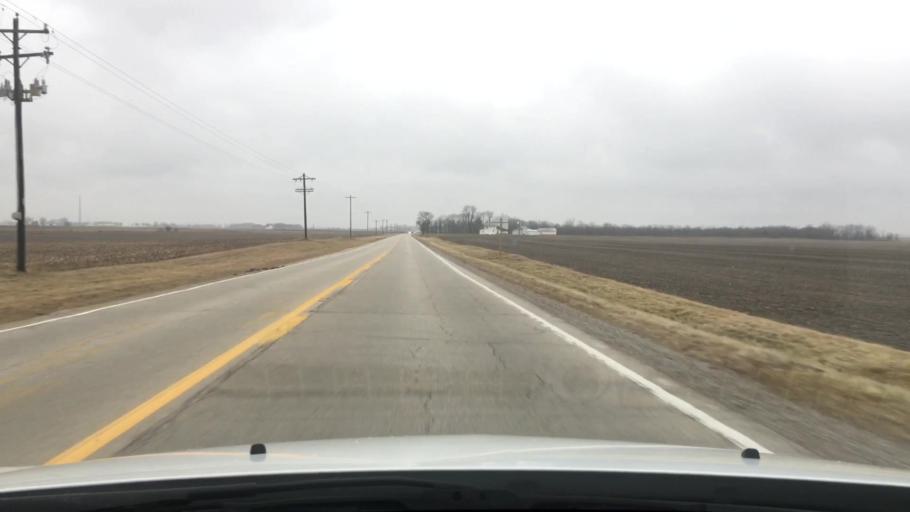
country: US
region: Illinois
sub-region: Iroquois County
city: Watseka
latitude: 40.8904
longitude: -87.7127
